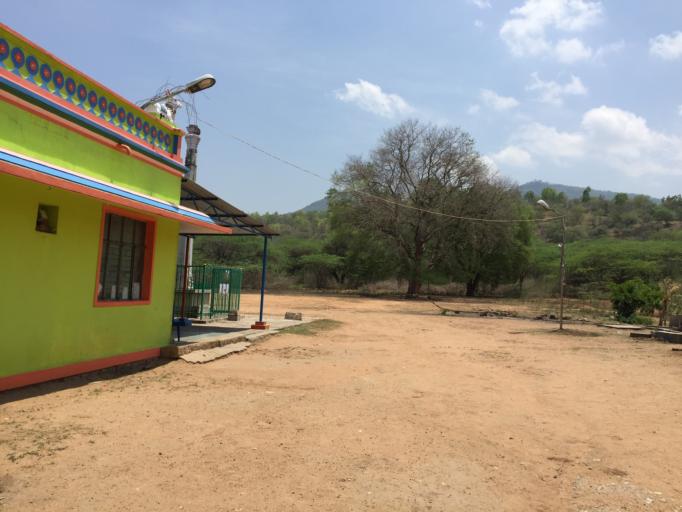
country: IN
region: Karnataka
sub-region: Mandya
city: Malavalli
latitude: 12.3138
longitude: 77.2785
